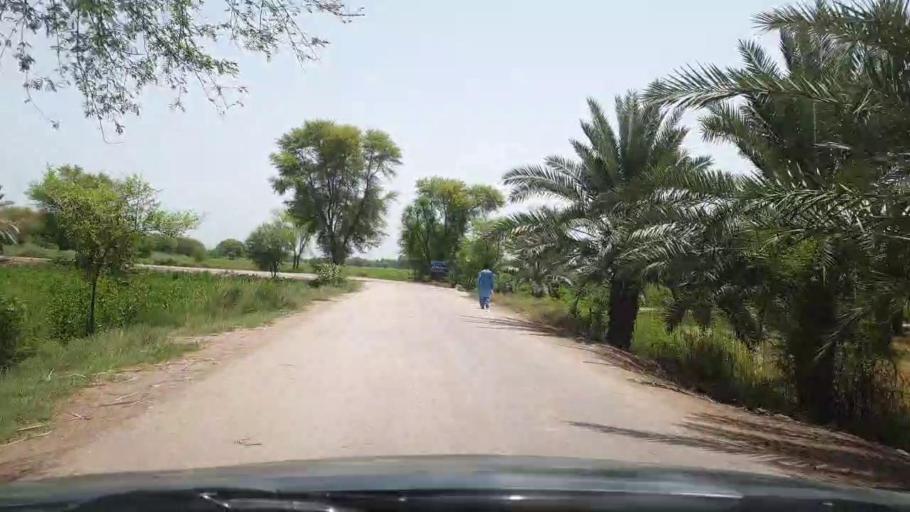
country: PK
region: Sindh
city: Pano Aqil
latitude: 27.8830
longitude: 69.1448
